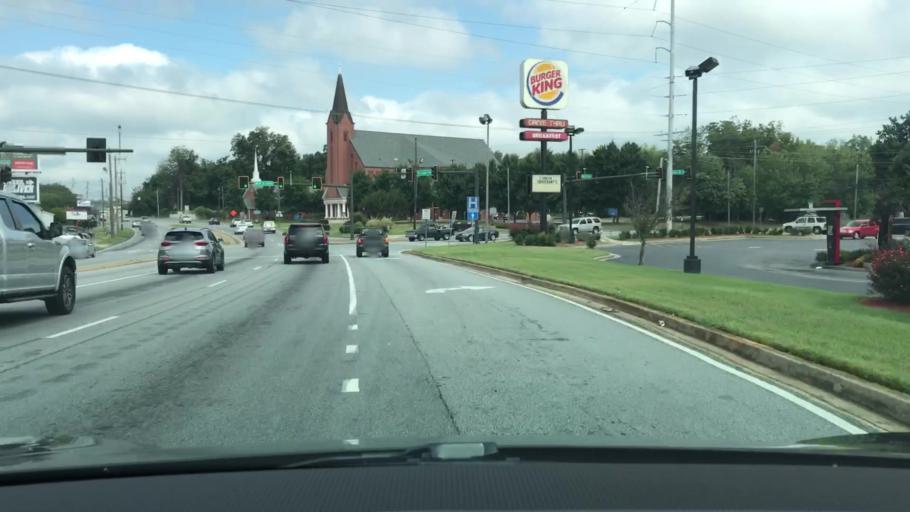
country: US
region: Georgia
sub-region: Hall County
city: Gainesville
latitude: 34.2937
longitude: -83.8155
